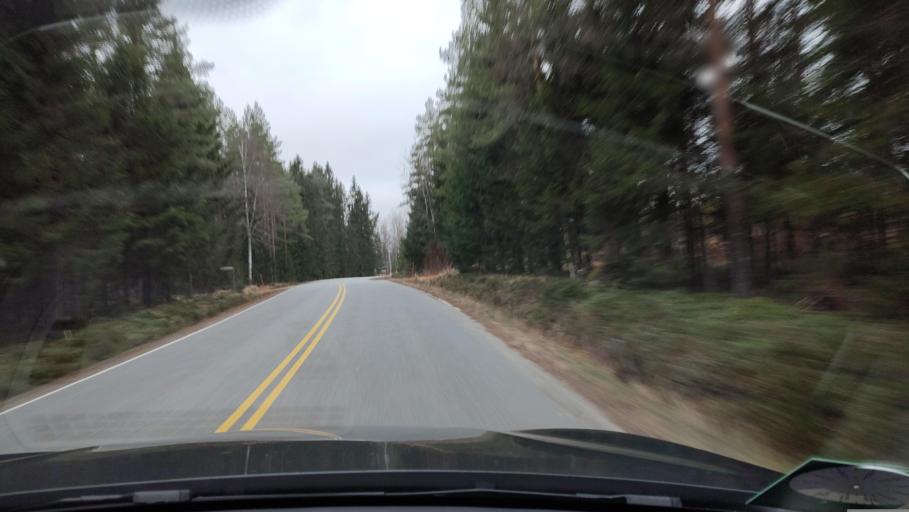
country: FI
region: Southern Ostrobothnia
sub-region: Suupohja
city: Karijoki
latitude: 62.2569
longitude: 21.7437
